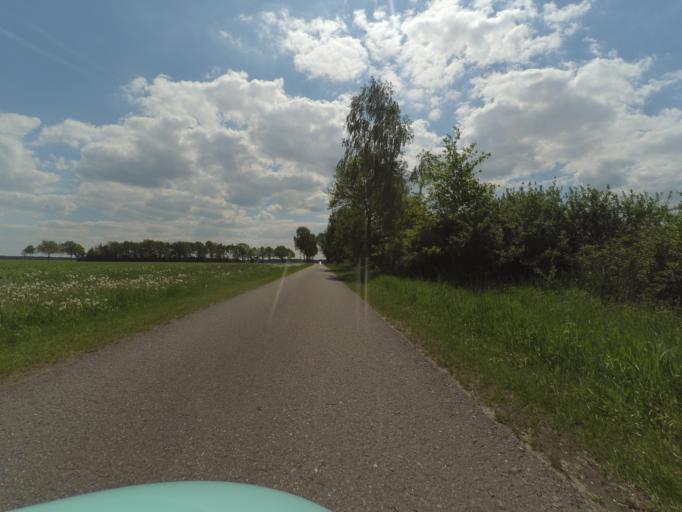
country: DE
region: Lower Saxony
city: Ummern
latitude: 52.5940
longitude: 10.4561
